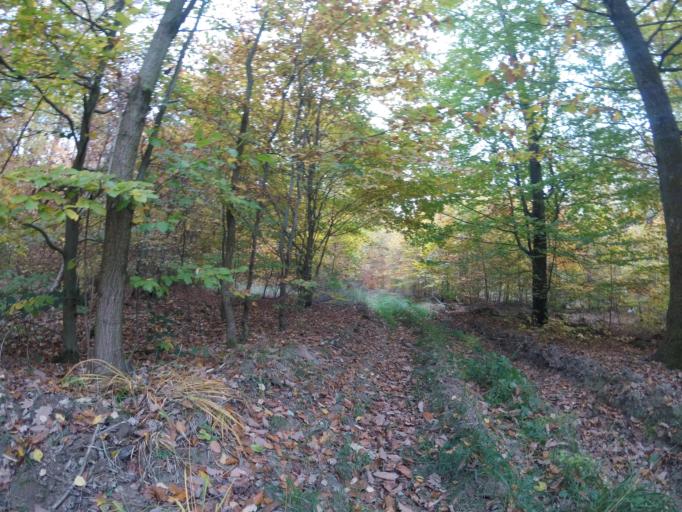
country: DE
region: Baden-Wuerttemberg
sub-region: Regierungsbezirk Stuttgart
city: Kirchberg an der Murr
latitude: 48.9785
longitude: 9.3539
